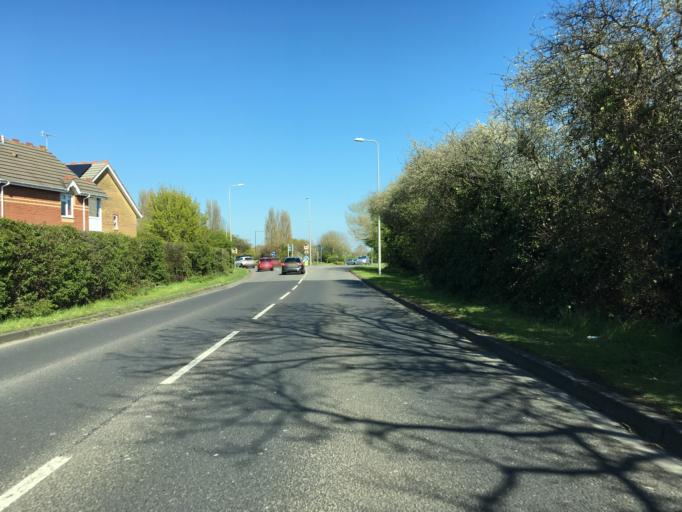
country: GB
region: England
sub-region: North Somerset
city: Portishead
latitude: 51.4772
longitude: -2.7566
